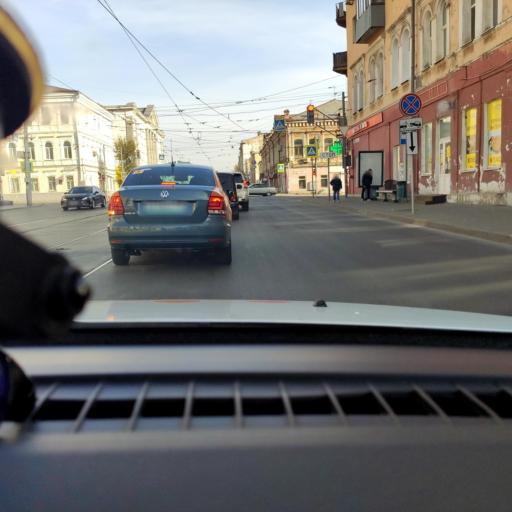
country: RU
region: Samara
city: Rozhdestveno
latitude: 53.1846
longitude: 50.0895
